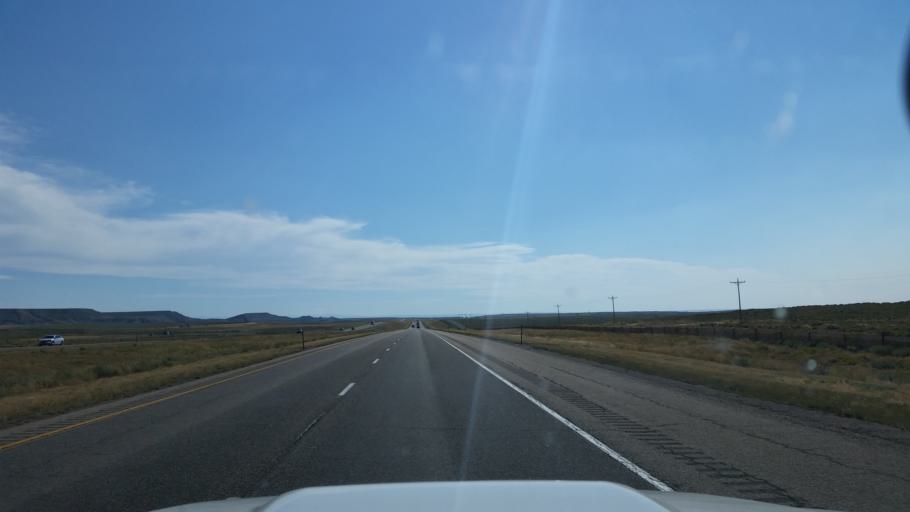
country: US
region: Wyoming
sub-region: Uinta County
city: Lyman
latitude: 41.4542
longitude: -110.0680
